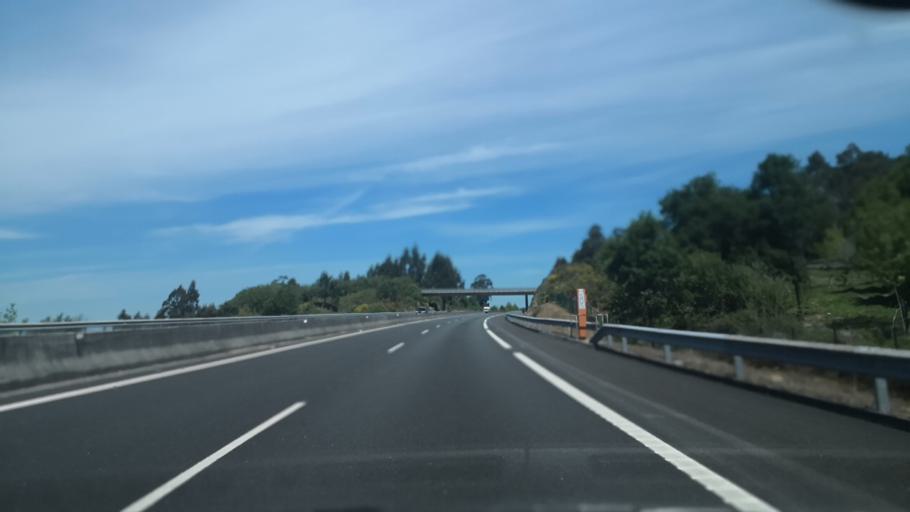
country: ES
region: Galicia
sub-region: Provincia de Pontevedra
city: Valga
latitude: 42.6529
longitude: -8.6507
